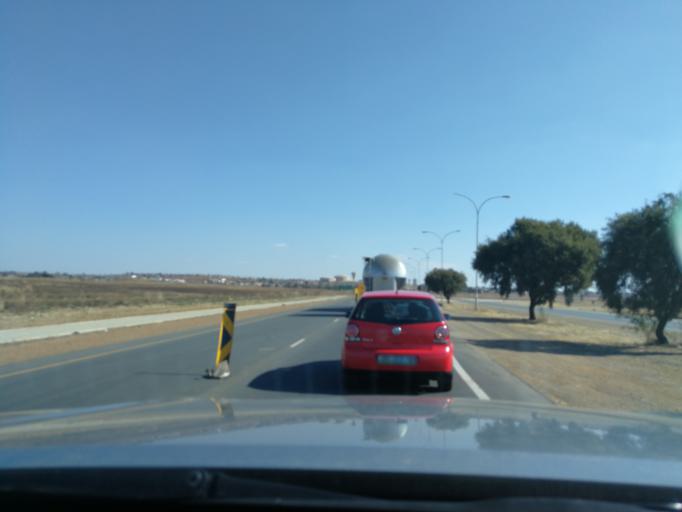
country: ZA
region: North-West
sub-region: Dr Kenneth Kaunda District Municipality
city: Klerksdorp
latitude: -26.8720
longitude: 26.6109
